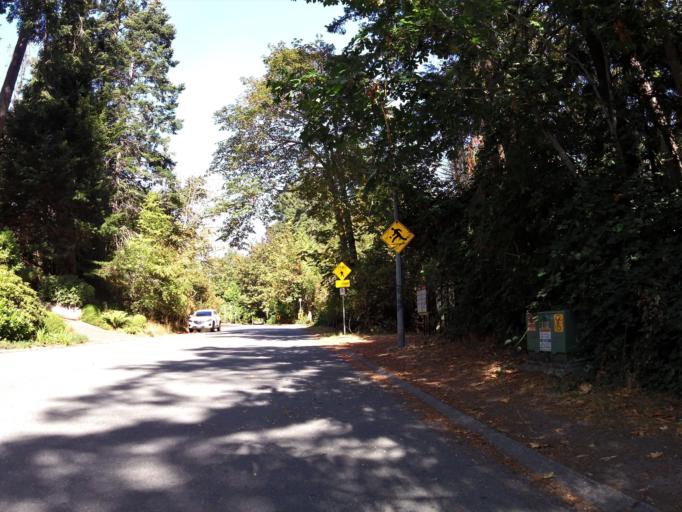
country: CA
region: British Columbia
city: Victoria
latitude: 48.5067
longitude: -123.3658
